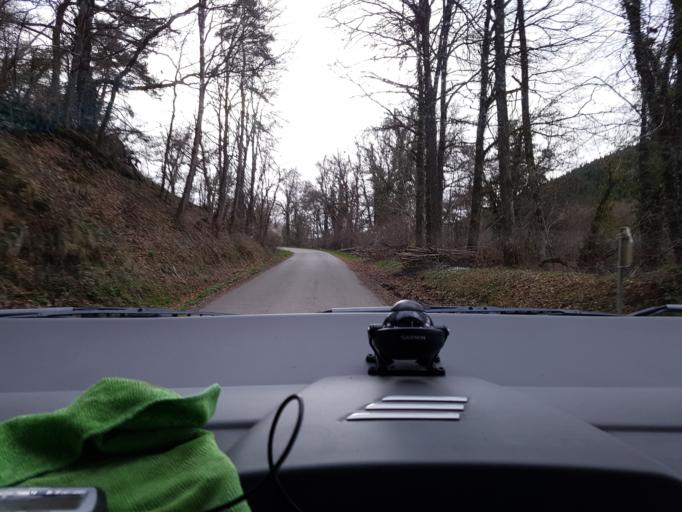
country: FR
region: Auvergne
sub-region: Departement du Puy-de-Dome
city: Saint-Ours
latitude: 45.8509
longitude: 2.8590
